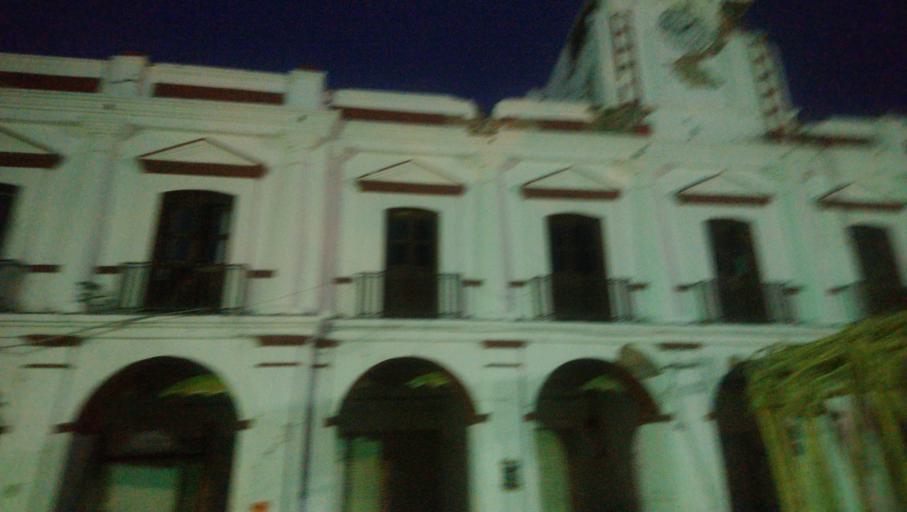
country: MX
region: Oaxaca
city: Juchitan de Zaragoza
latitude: 16.4333
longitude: -95.0218
